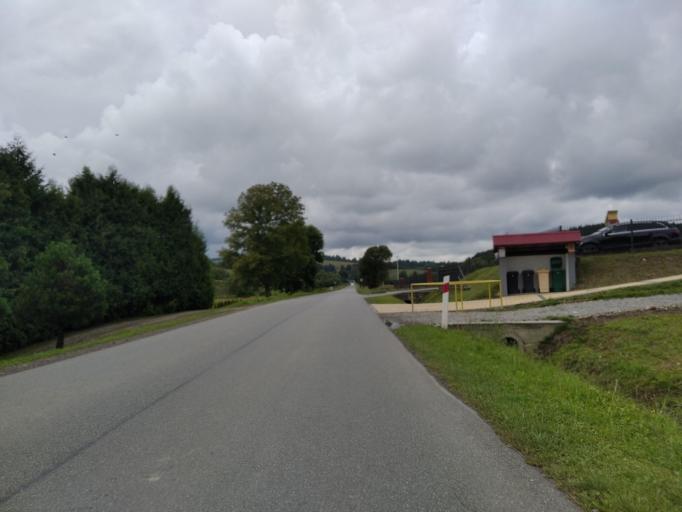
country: PL
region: Subcarpathian Voivodeship
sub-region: Powiat przemyski
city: Bircza
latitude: 49.6984
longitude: 22.3780
